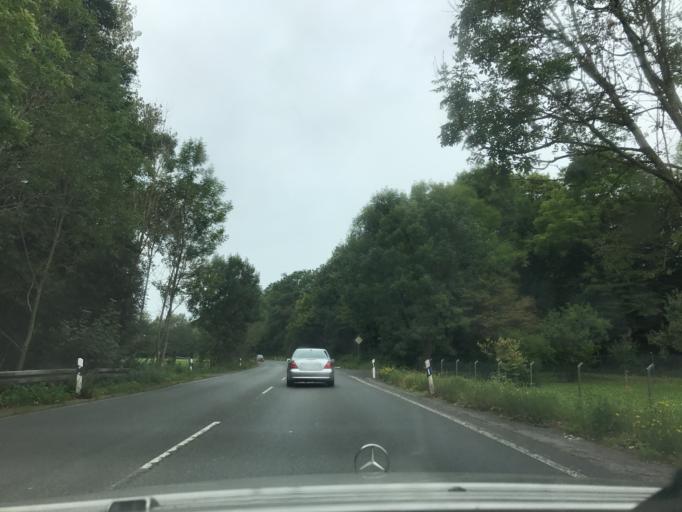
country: DE
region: North Rhine-Westphalia
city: Wetter (Ruhr)
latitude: 51.3514
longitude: 7.3992
